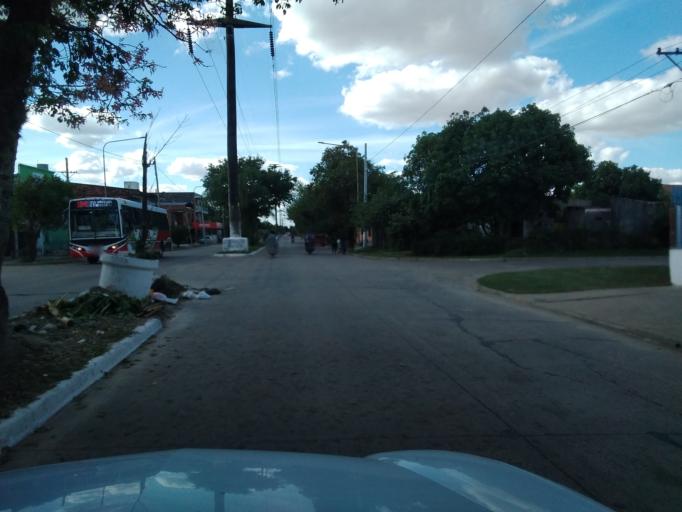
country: AR
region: Corrientes
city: Corrientes
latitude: -27.4910
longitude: -58.8381
